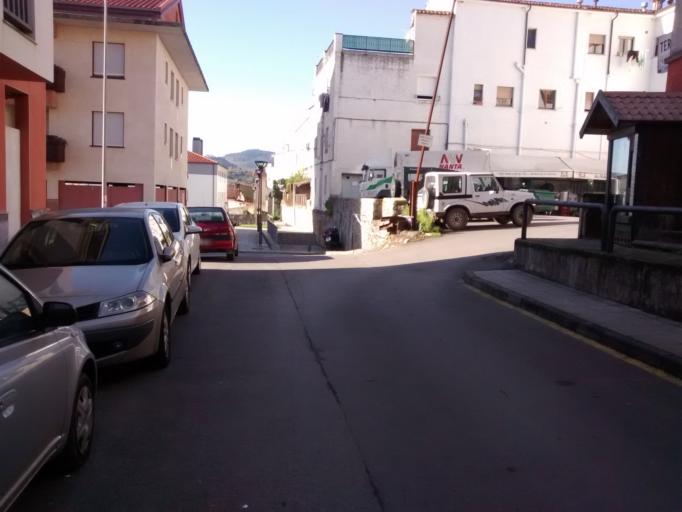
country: ES
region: Asturias
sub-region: Province of Asturias
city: Colunga
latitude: 43.4848
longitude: -5.2702
